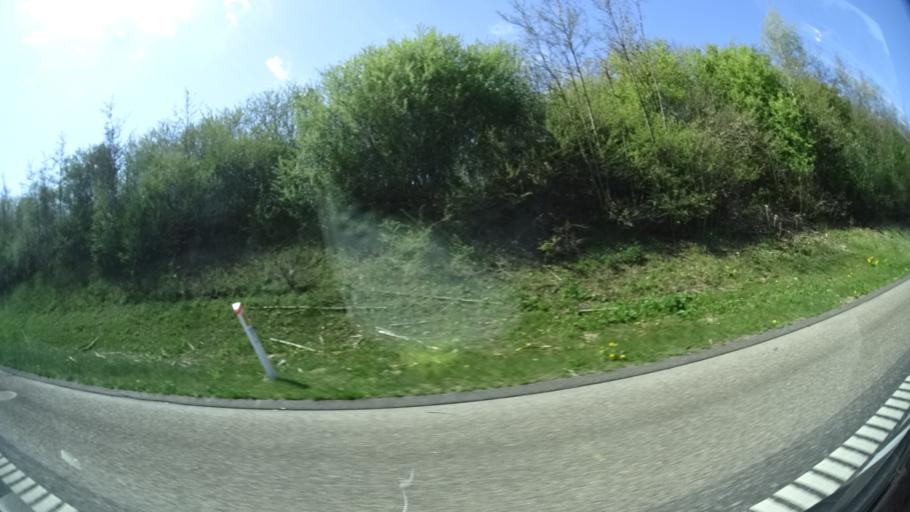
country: DK
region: Central Jutland
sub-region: Arhus Kommune
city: Trige
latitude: 56.2365
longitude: 10.1250
